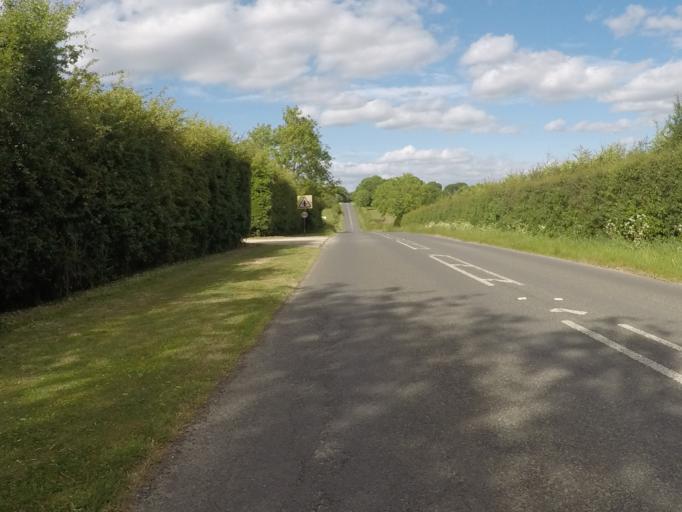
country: GB
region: England
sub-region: Oxfordshire
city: Charlbury
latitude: 51.8365
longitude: -1.4983
